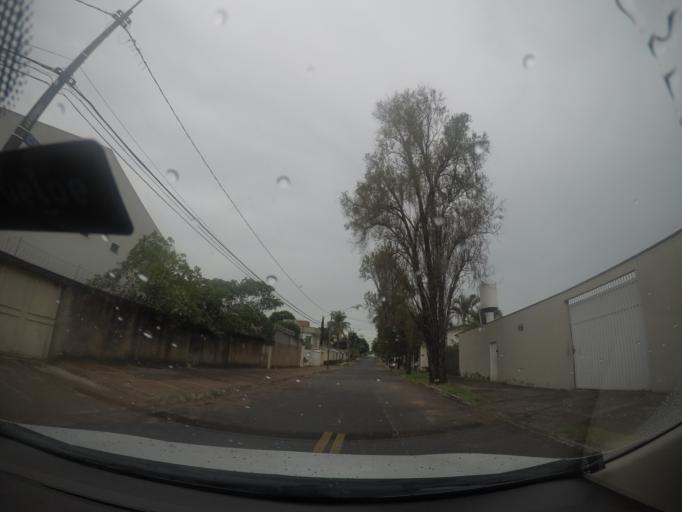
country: BR
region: Goias
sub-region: Goiania
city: Goiania
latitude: -16.6505
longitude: -49.2332
